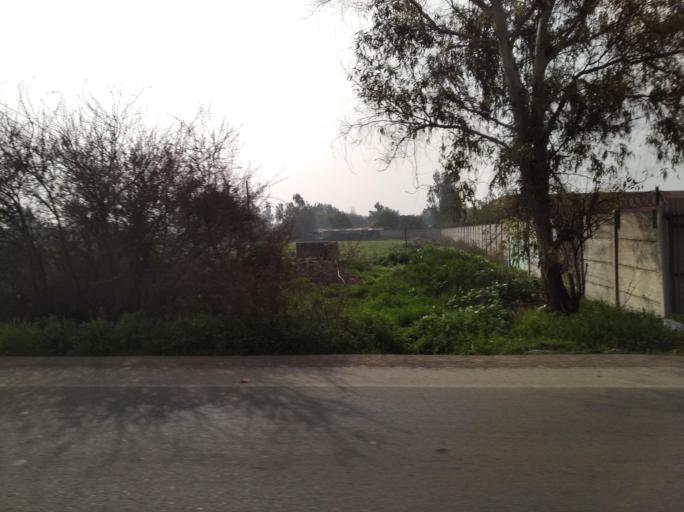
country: CL
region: Santiago Metropolitan
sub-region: Provincia de Chacabuco
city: Lampa
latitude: -33.2962
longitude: -70.8656
